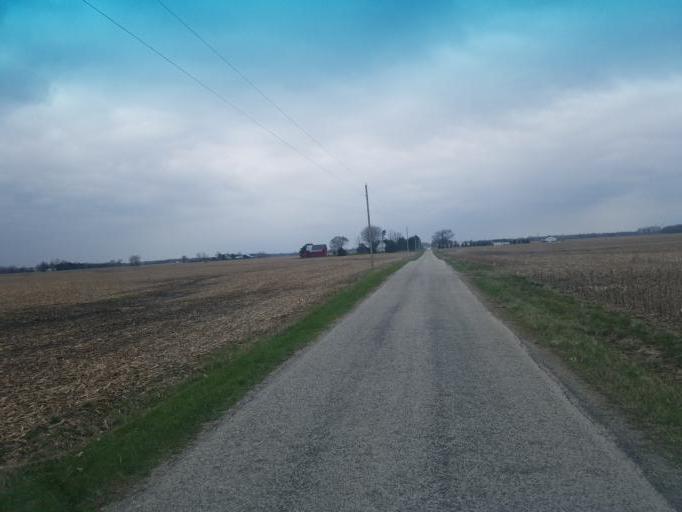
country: US
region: Ohio
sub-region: Marion County
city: Prospect
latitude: 40.4404
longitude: -83.1488
